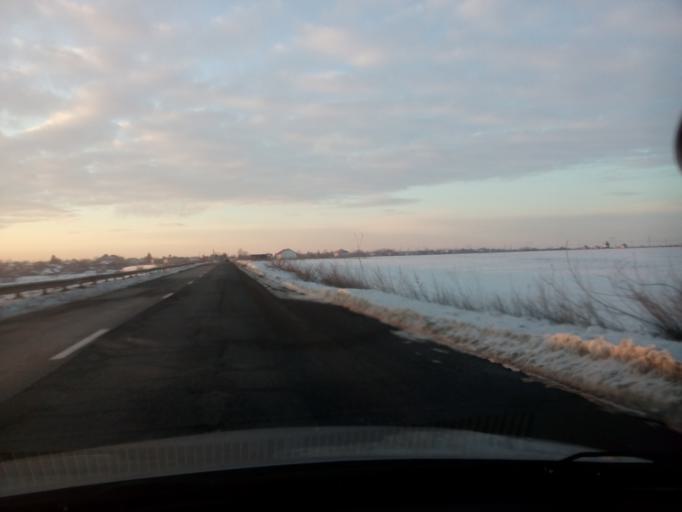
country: RO
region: Calarasi
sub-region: Comuna Soldanu
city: Soldanu
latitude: 44.2189
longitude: 26.5371
